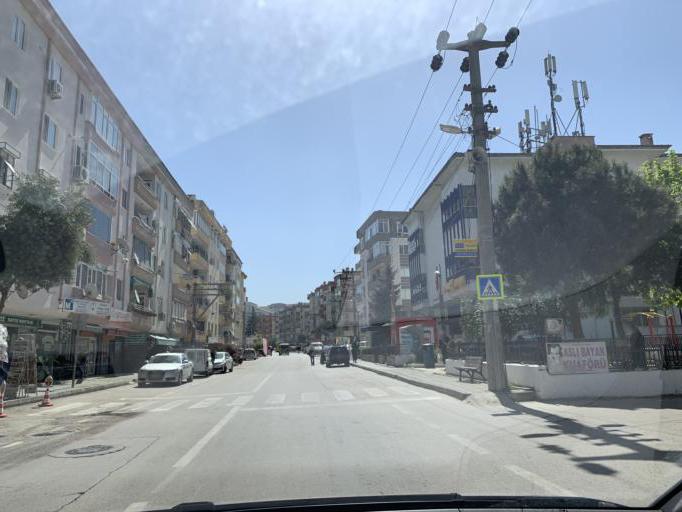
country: TR
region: Bursa
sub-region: Mudanya
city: Mudanya
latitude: 40.3551
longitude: 28.9237
